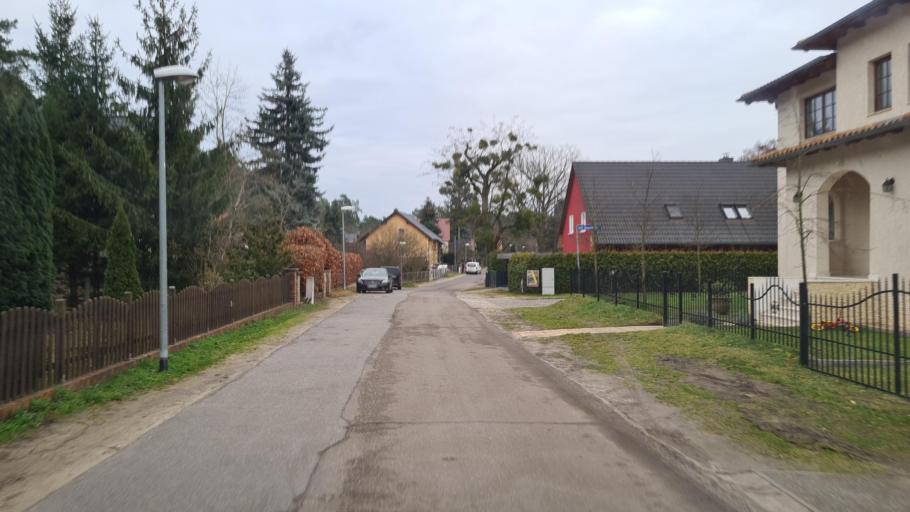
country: DE
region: Brandenburg
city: Stahnsdorf
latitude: 52.3791
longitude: 13.1868
